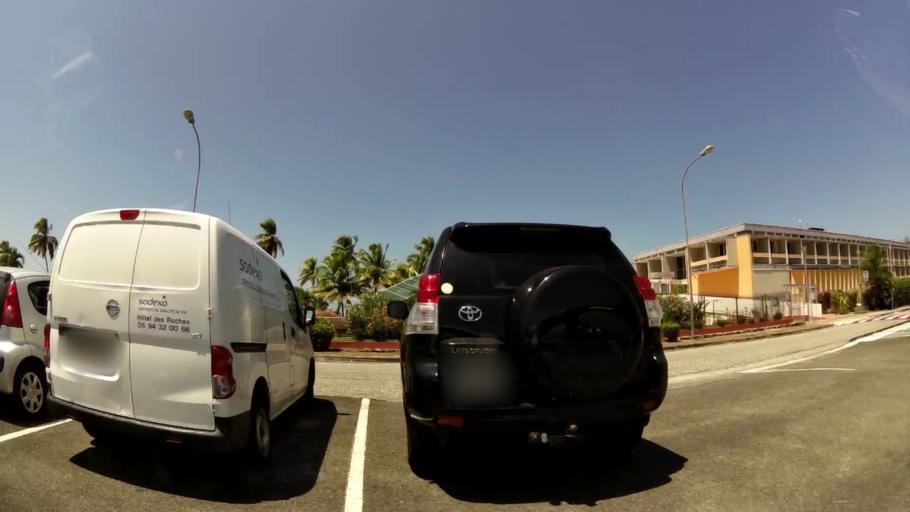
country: GF
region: Guyane
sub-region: Guyane
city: Kourou
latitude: 5.1605
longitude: -52.6282
